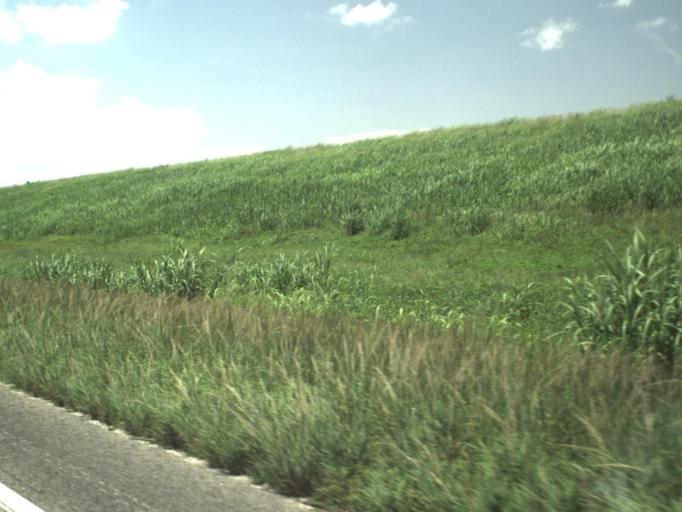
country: US
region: Florida
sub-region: Palm Beach County
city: South Bay
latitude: 26.6886
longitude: -80.7627
